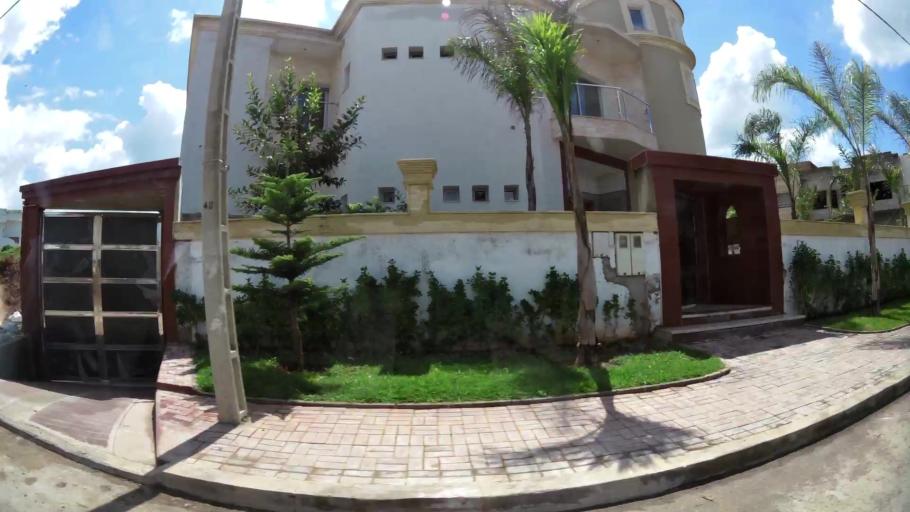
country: MA
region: Chaouia-Ouardigha
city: Nouaseur
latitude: 33.3967
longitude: -7.5647
